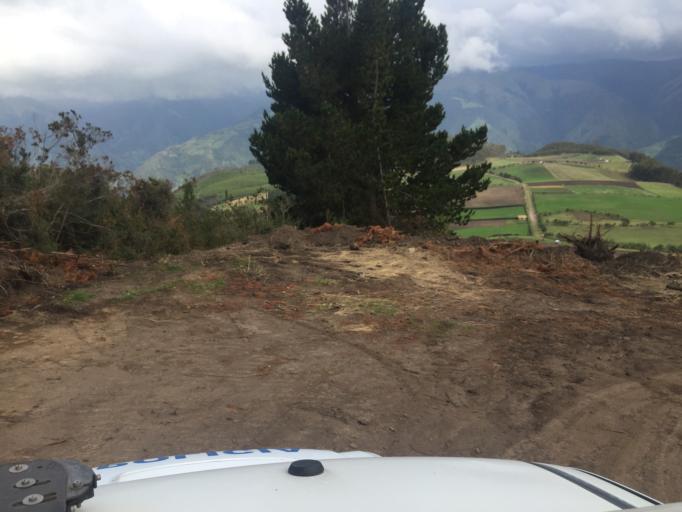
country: EC
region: Imbabura
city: Ibarra
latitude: 0.2284
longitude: -78.1231
